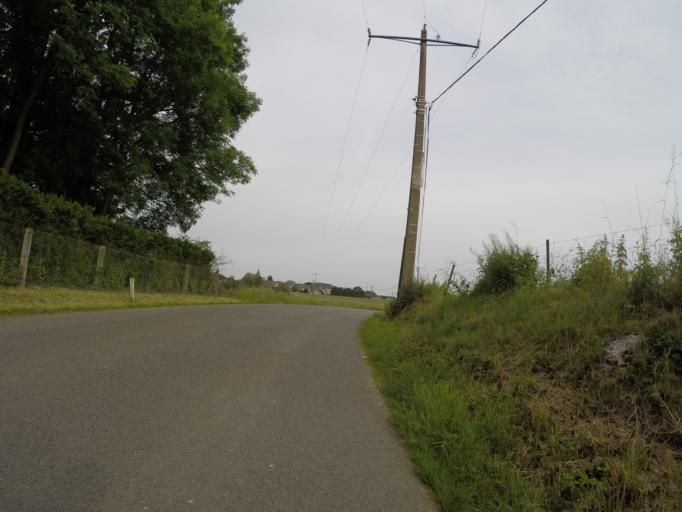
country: BE
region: Wallonia
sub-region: Province de Namur
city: Dinant
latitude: 50.2940
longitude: 4.9554
